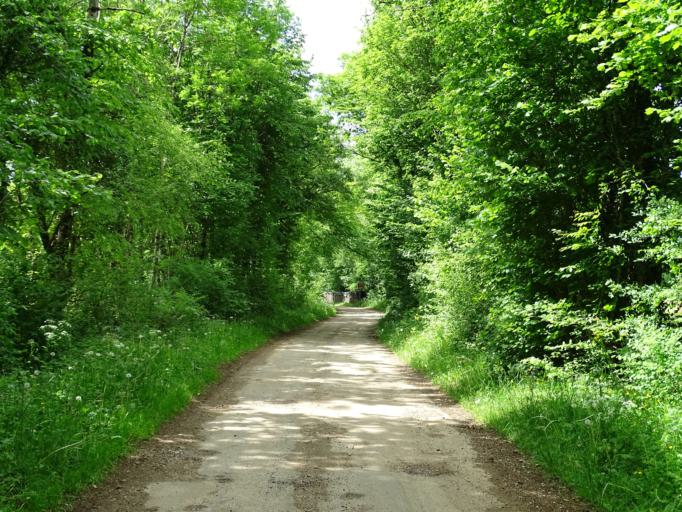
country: FR
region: Franche-Comte
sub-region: Departement du Doubs
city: Levier
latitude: 47.0093
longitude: 6.0163
